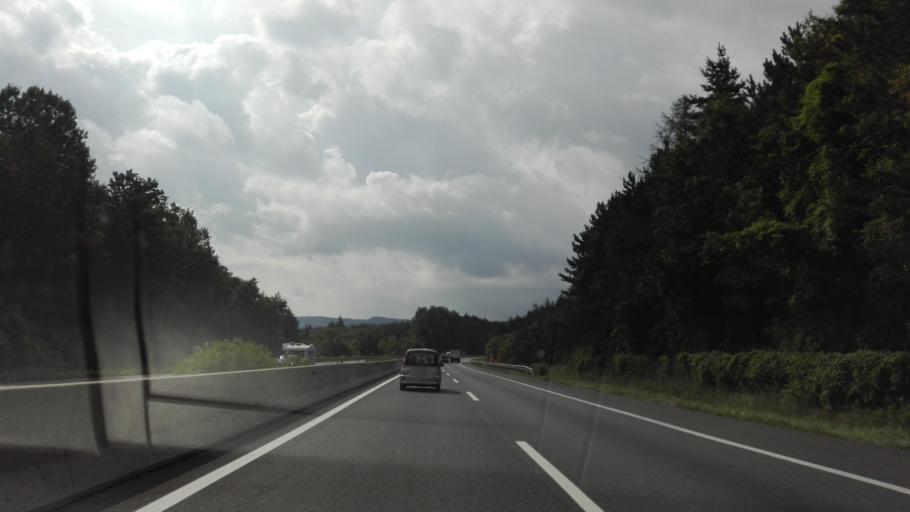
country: AT
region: Lower Austria
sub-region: Politischer Bezirk Baden
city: Klausen-Leopoldsdorf
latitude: 48.1103
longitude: 15.9770
